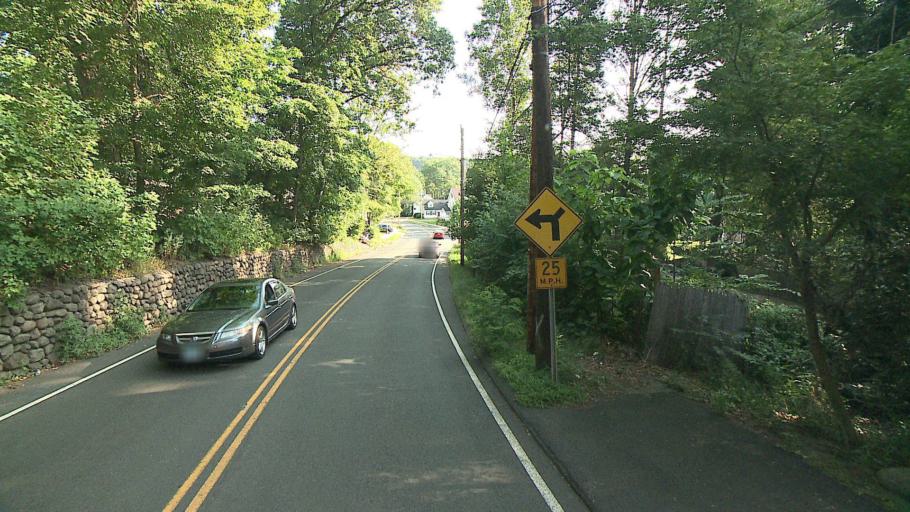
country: US
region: Connecticut
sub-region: New Haven County
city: New Haven
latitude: 41.3239
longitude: -72.9693
